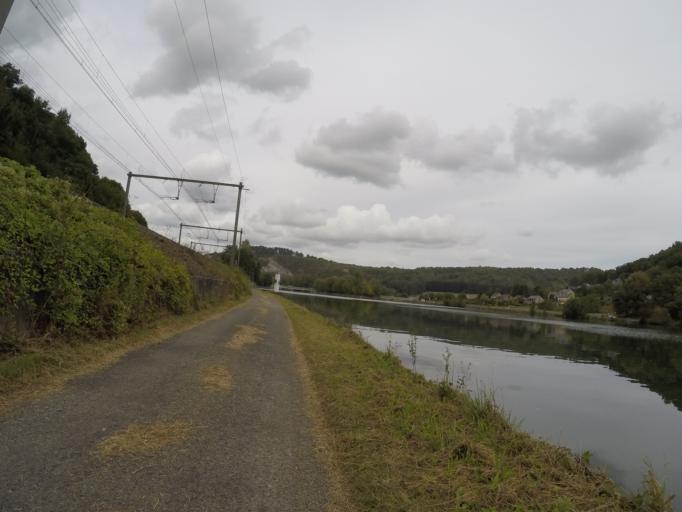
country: BE
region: Wallonia
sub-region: Province de Namur
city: Anhee
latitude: 50.2923
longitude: 4.8940
